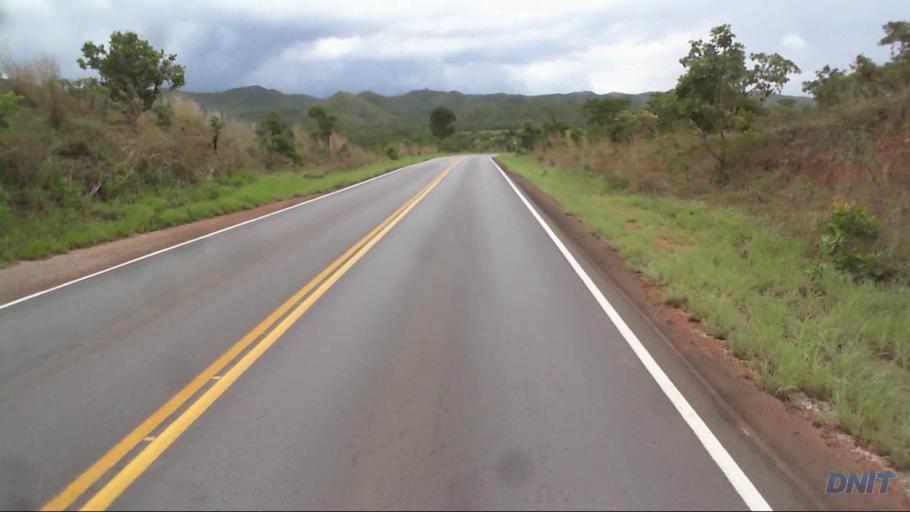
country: BR
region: Goias
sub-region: Padre Bernardo
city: Padre Bernardo
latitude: -15.4319
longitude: -48.1936
